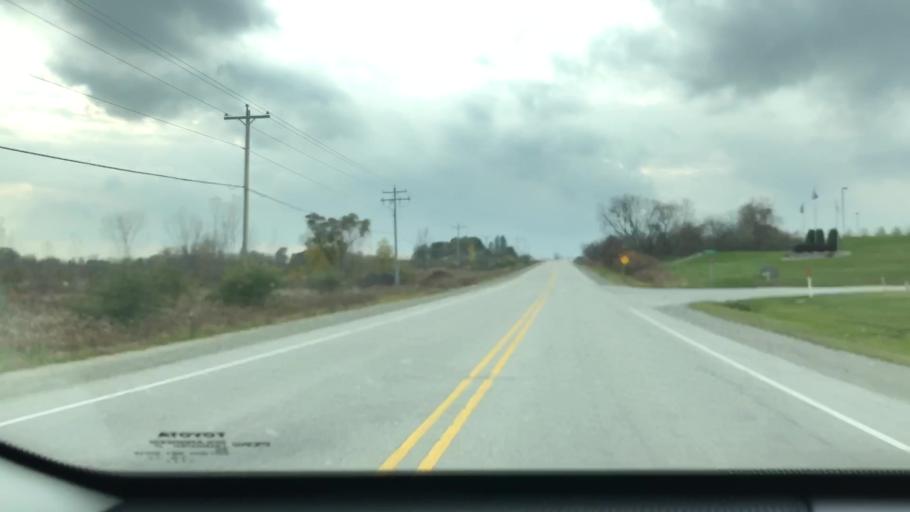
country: US
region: Wisconsin
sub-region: Brown County
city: Oneida
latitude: 44.5100
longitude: -88.1633
